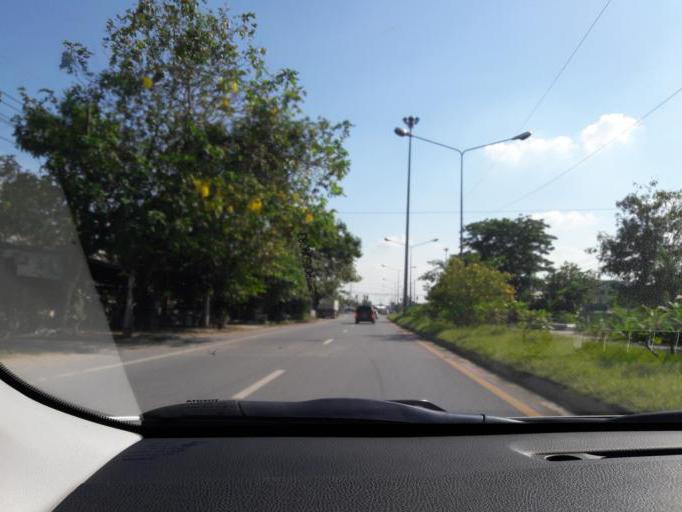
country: TH
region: Ang Thong
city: Ang Thong
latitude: 14.5793
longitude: 100.4528
